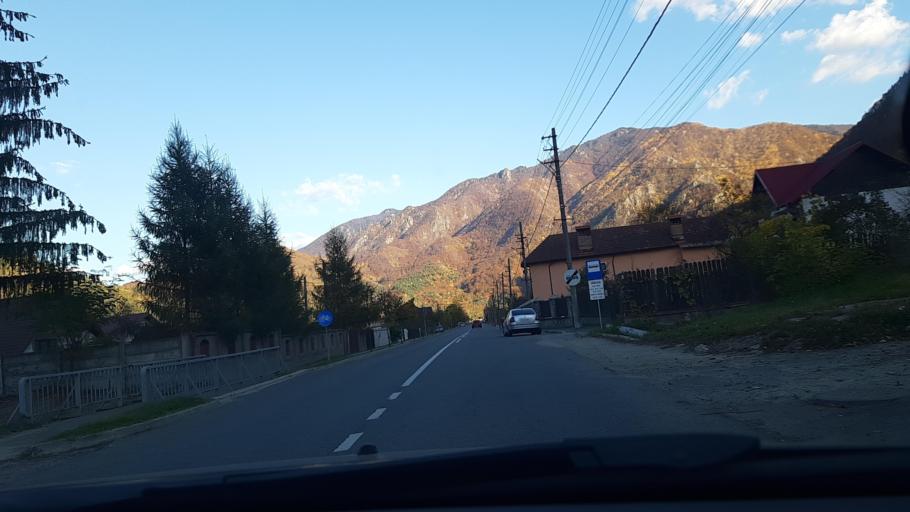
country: RO
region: Valcea
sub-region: Comuna Brezoi
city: Brezoi
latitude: 45.3333
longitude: 24.2581
